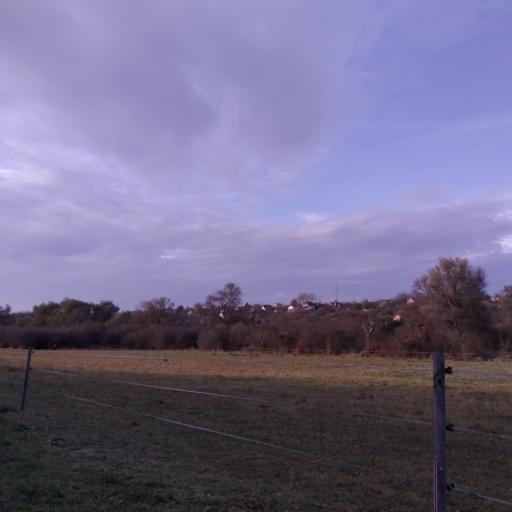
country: HU
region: Pest
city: Pomaz
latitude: 47.6281
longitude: 19.0252
